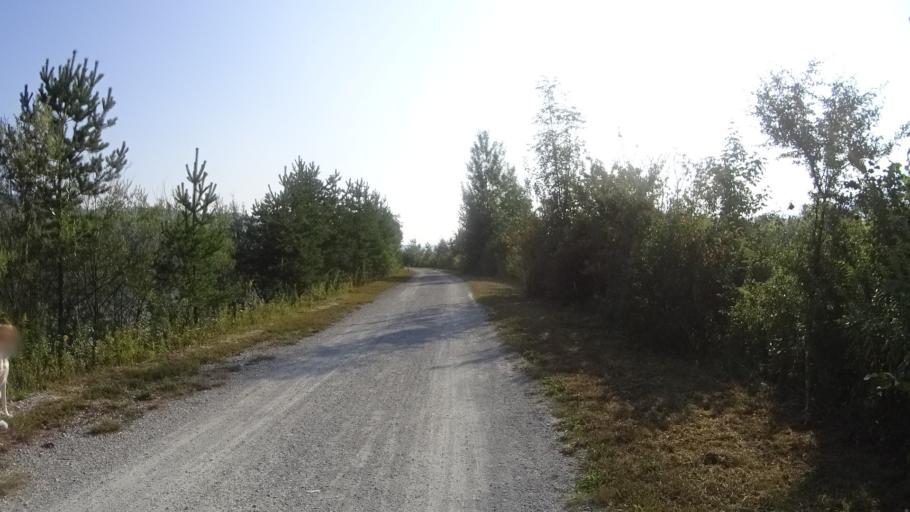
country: AT
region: Carinthia
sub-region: Politischer Bezirk Klagenfurt Land
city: Feistritz im Rosental
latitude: 46.5312
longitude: 14.1671
